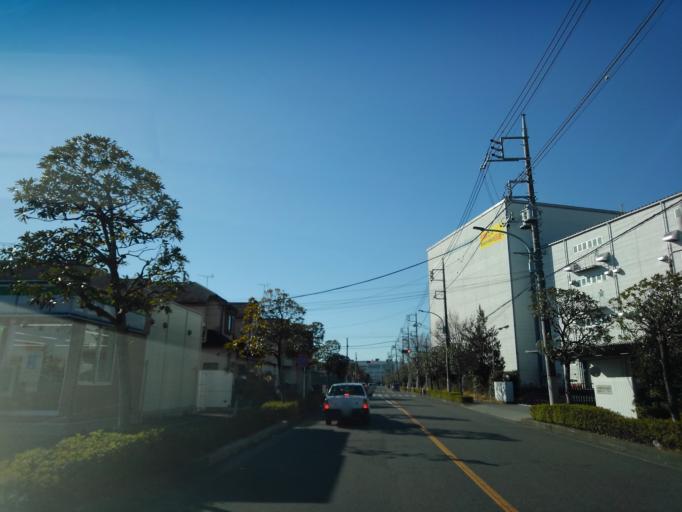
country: JP
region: Tokyo
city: Fussa
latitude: 35.7798
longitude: 139.3232
